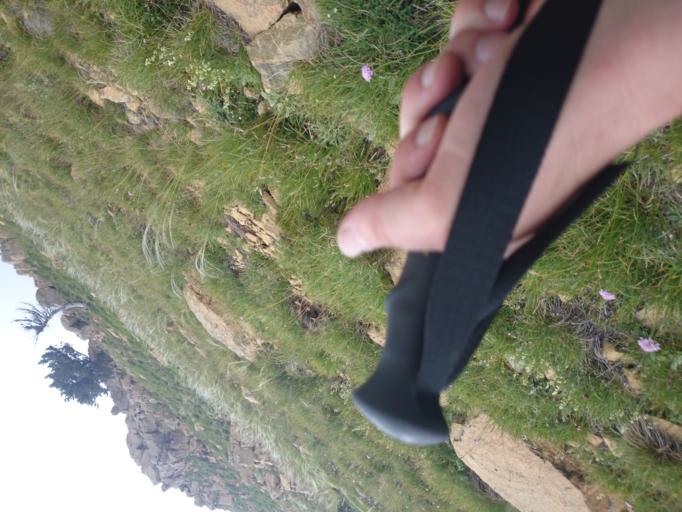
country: AL
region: Diber
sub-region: Rrethi i Dibres
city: Fushe-Lure
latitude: 41.7840
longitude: 20.1829
